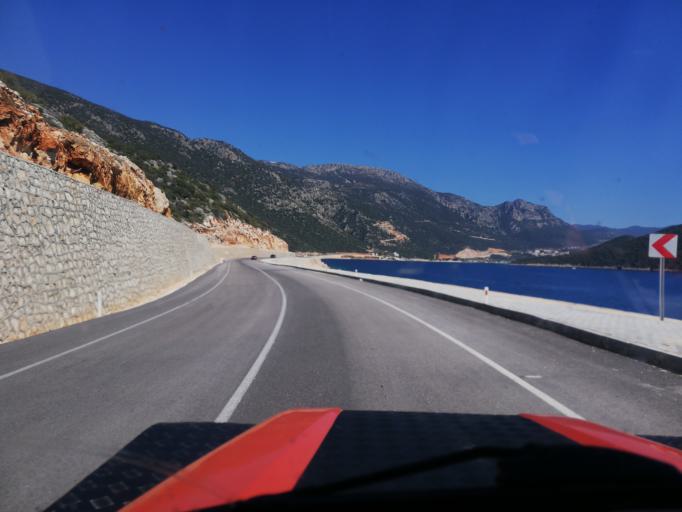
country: TR
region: Antalya
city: Kas
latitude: 36.2028
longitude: 29.5958
